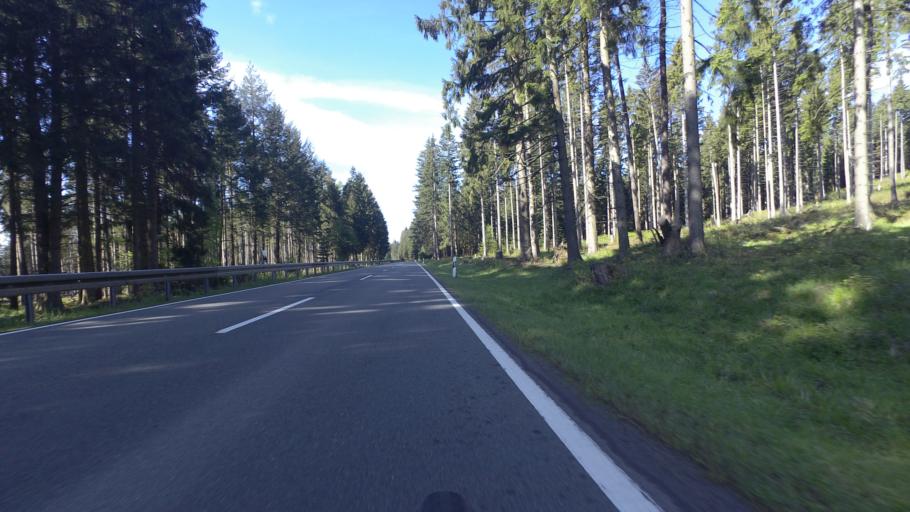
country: DE
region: Saxony-Anhalt
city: Darlingerode
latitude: 51.7618
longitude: 10.7181
